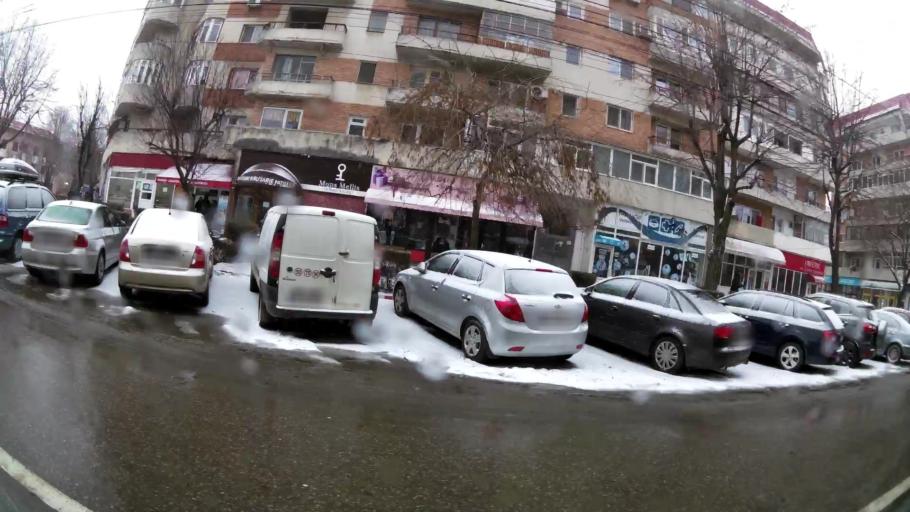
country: RO
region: Dambovita
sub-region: Municipiul Targoviste
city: Targoviste
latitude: 44.9276
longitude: 25.4651
